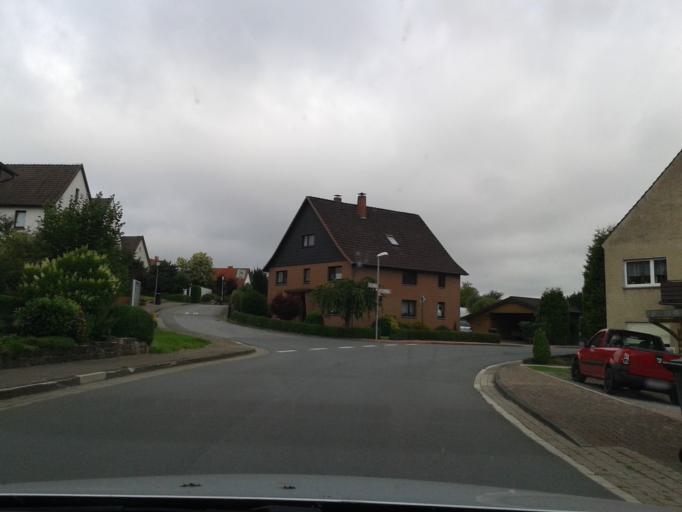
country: DE
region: North Rhine-Westphalia
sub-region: Regierungsbezirk Detmold
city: Barntrup
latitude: 52.0071
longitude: 9.0597
